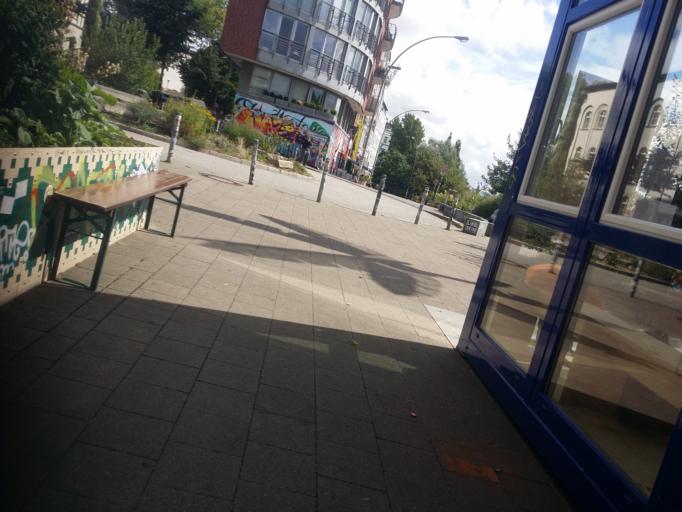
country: DE
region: Hamburg
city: St. Pauli
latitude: 53.5463
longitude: 9.9574
